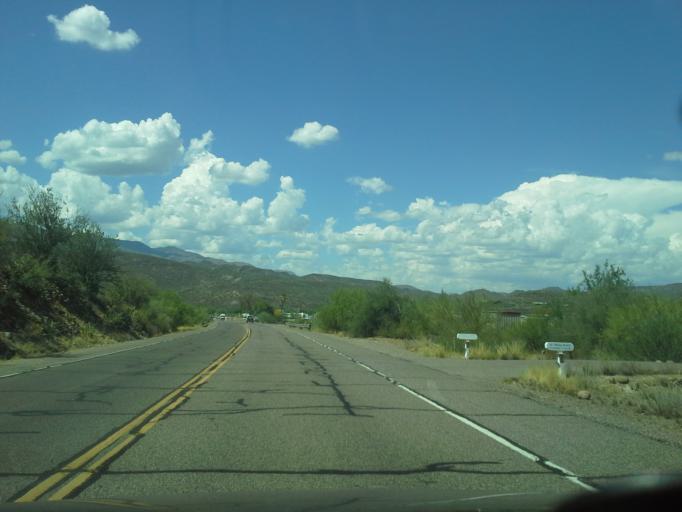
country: US
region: Arizona
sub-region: Yavapai County
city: Black Canyon City
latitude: 34.0631
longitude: -112.1479
